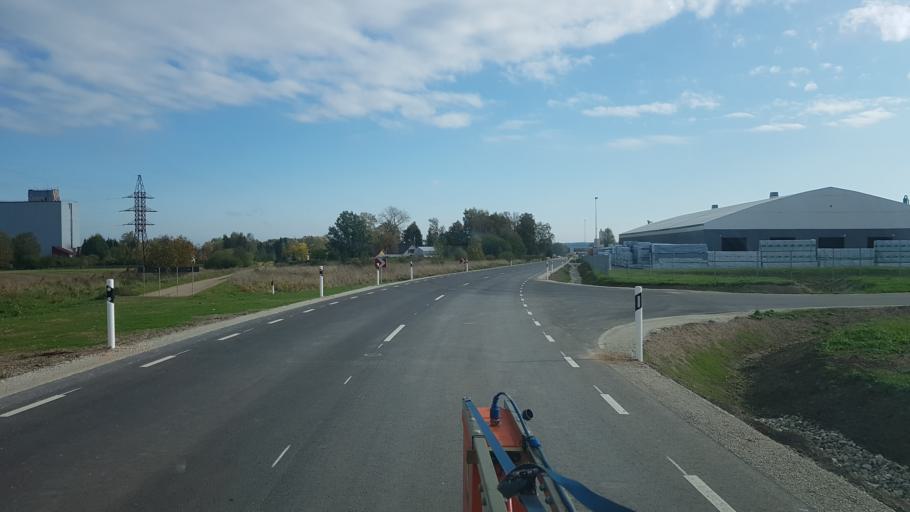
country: EE
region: Tartu
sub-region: UElenurme vald
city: Ulenurme
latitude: 58.2942
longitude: 26.7019
